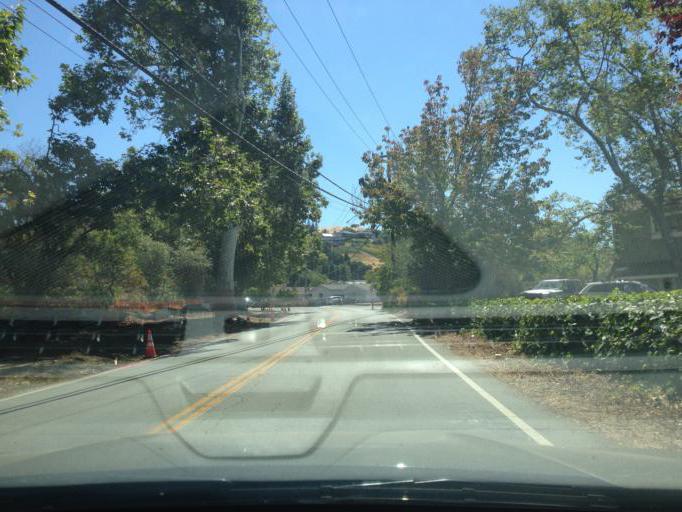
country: US
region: California
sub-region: Santa Clara County
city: East Foothills
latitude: 37.3938
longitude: -121.8316
